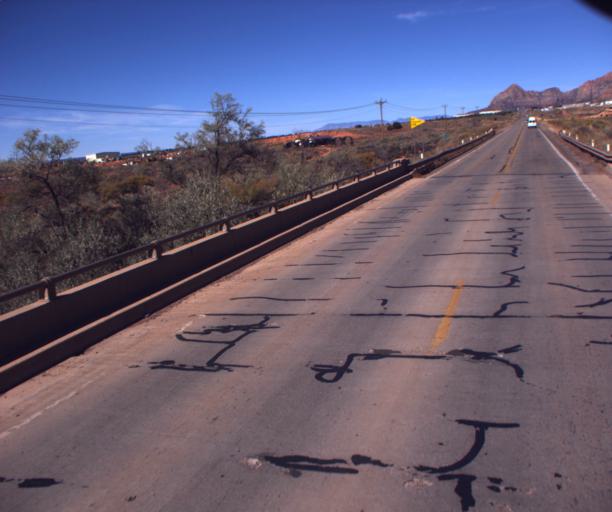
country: US
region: Arizona
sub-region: Mohave County
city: Colorado City
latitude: 36.9881
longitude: -112.9891
